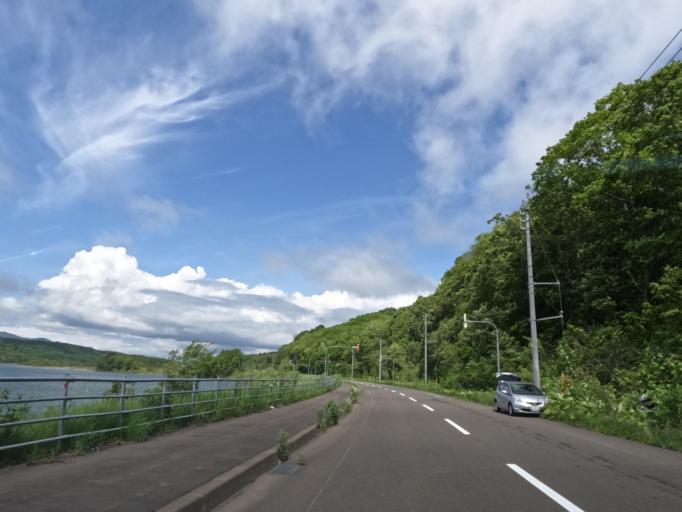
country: JP
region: Hokkaido
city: Tobetsu
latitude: 43.3627
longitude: 141.5706
